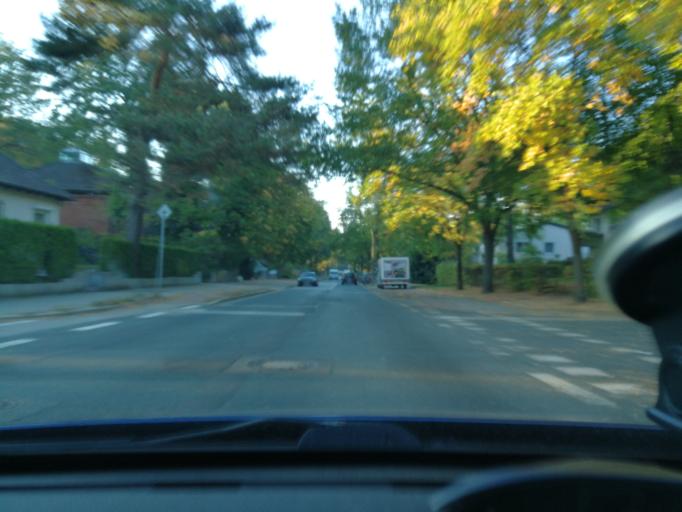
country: DE
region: Hamburg
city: Harburg
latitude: 53.4669
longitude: 9.9525
